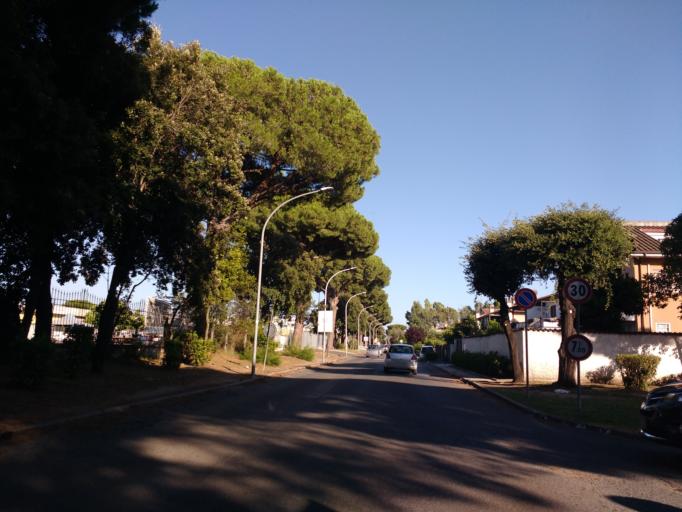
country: IT
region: Latium
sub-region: Citta metropolitana di Roma Capitale
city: Acilia-Castel Fusano-Ostia Antica
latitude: 41.7595
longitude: 12.3635
